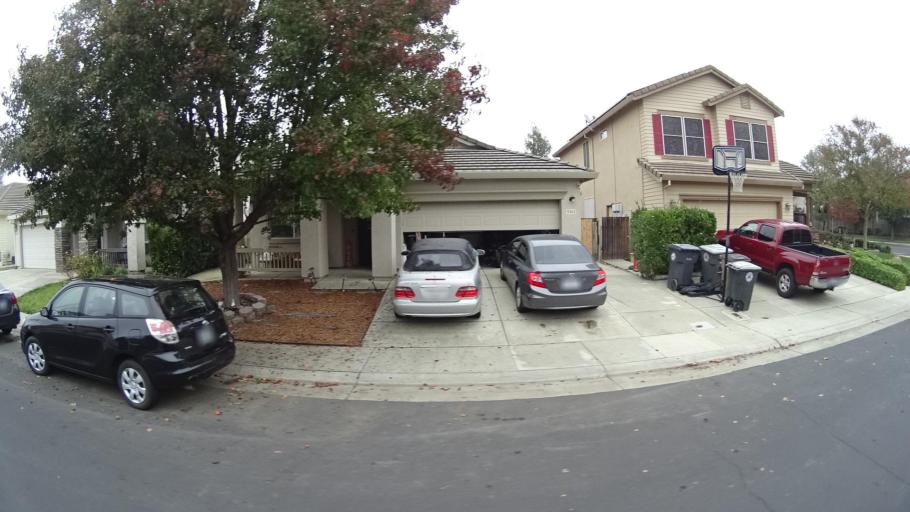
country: US
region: California
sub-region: Sacramento County
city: Elk Grove
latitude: 38.4130
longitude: -121.3462
